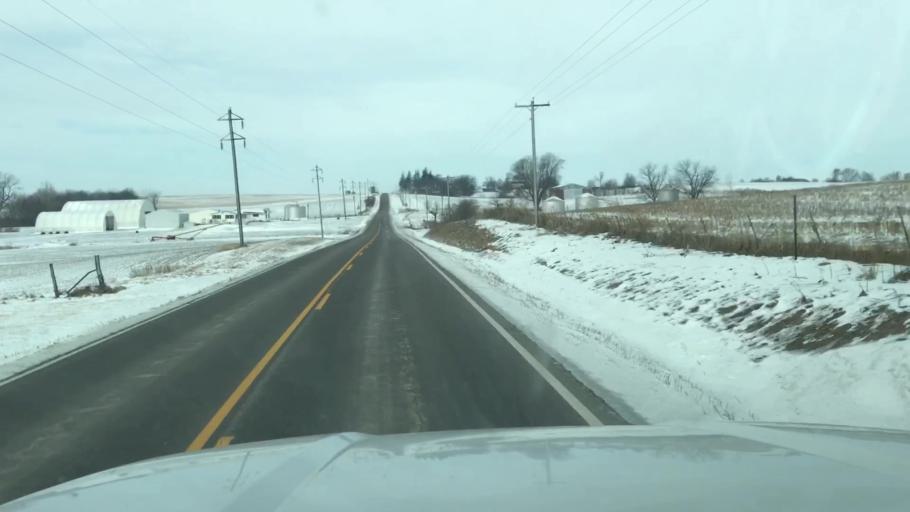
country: US
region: Missouri
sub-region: Holt County
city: Mound City
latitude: 40.1301
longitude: -95.1217
